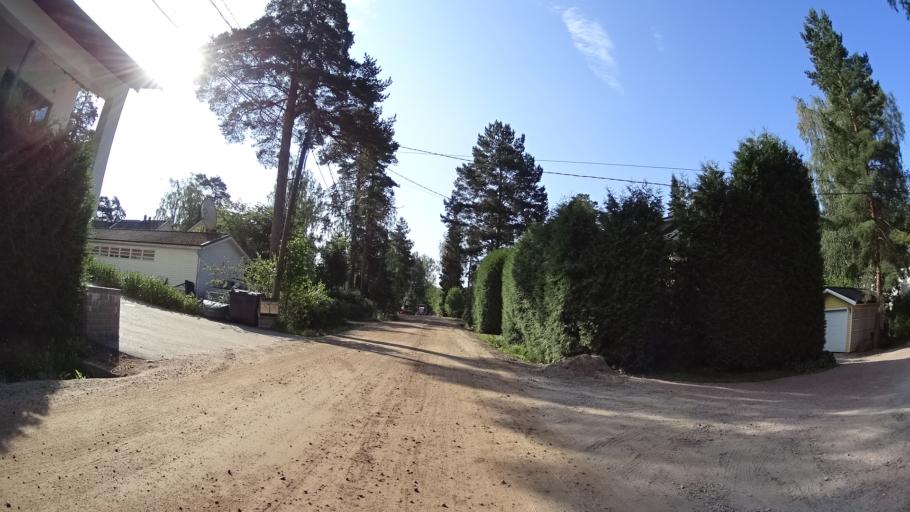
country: FI
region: Uusimaa
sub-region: Helsinki
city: Otaniemi
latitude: 60.1951
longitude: 24.8008
